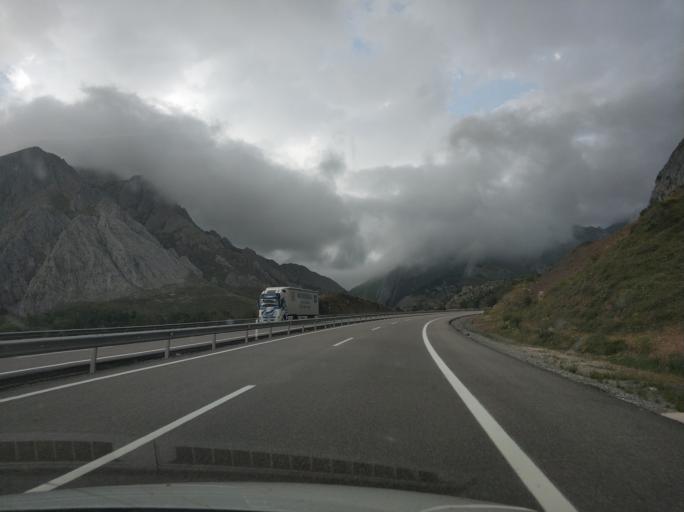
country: ES
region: Castille and Leon
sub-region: Provincia de Leon
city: Sena de Luna
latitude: 42.9239
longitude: -5.8711
